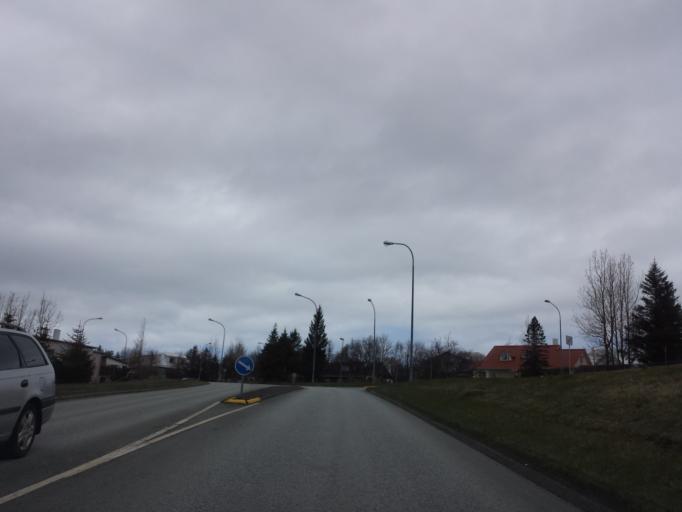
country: IS
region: Capital Region
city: Kopavogur
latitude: 64.1095
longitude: -21.8855
